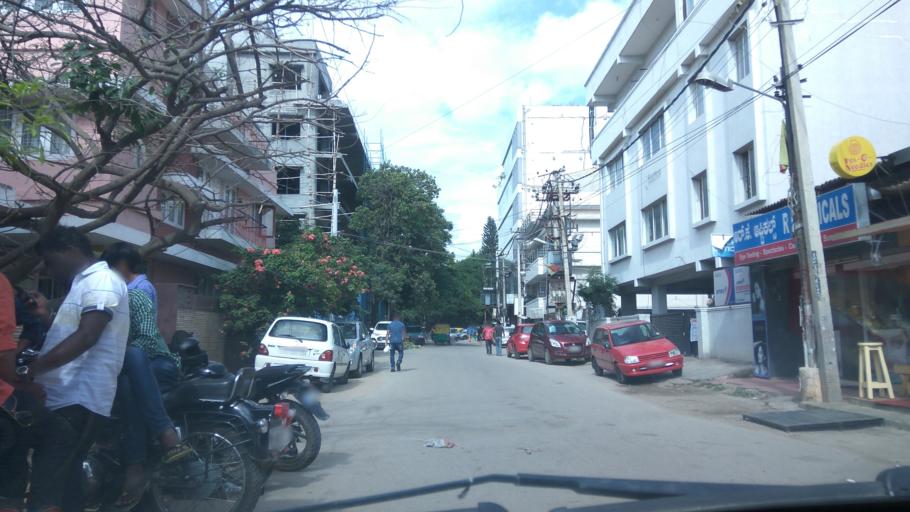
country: IN
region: Karnataka
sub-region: Bangalore Urban
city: Bangalore
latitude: 12.9685
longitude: 77.6403
